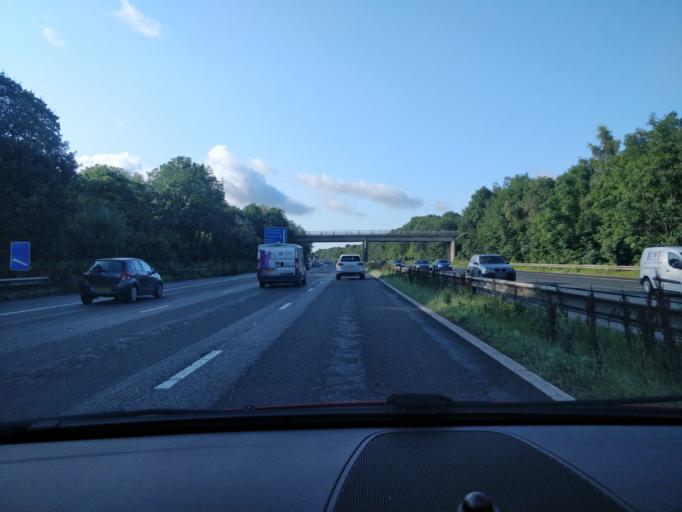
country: GB
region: England
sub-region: Knowsley
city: Knowsley
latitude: 53.4420
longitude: -2.8583
